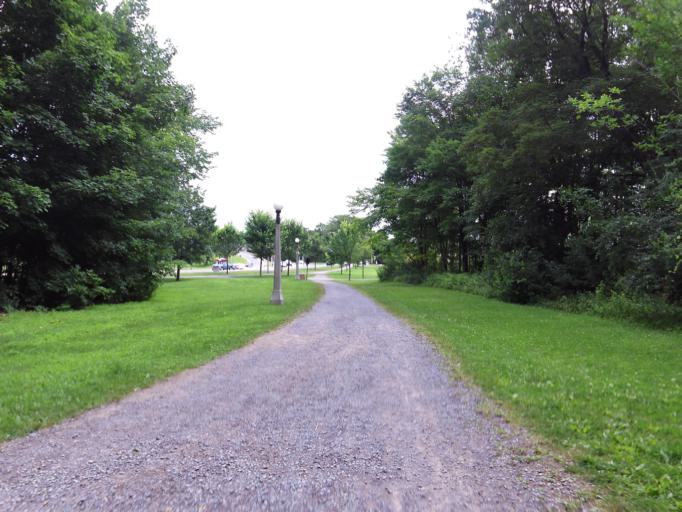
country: CA
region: Ontario
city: Ottawa
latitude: 45.3894
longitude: -75.7377
